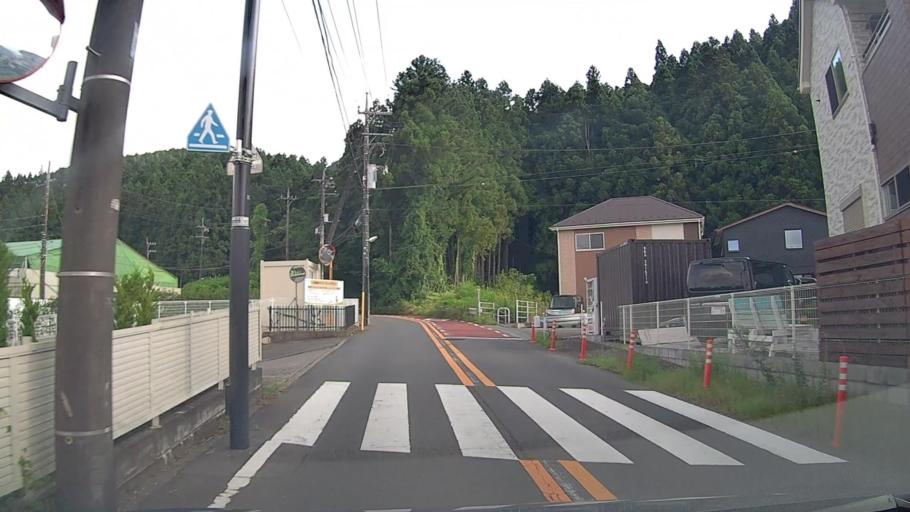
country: JP
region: Tokyo
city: Itsukaichi
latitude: 35.7218
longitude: 139.2262
